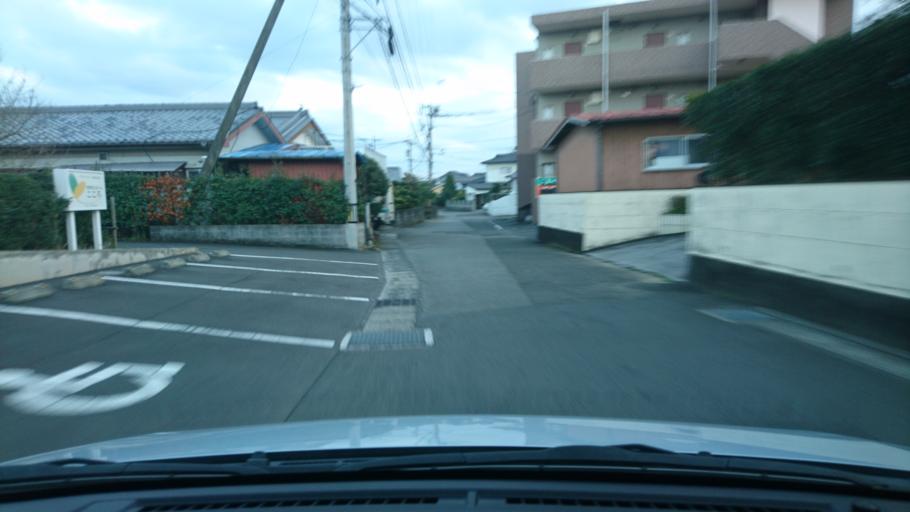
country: JP
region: Miyazaki
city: Miyazaki-shi
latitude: 31.8557
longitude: 131.4309
